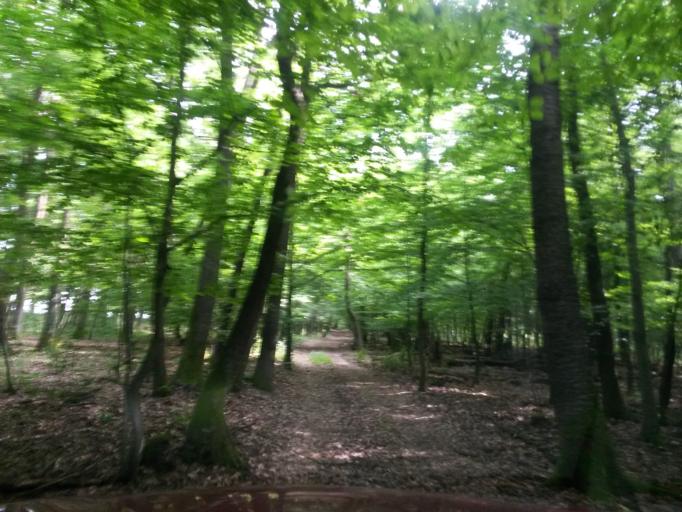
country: SK
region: Kosicky
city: Moldava nad Bodvou
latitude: 48.6322
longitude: 21.1018
